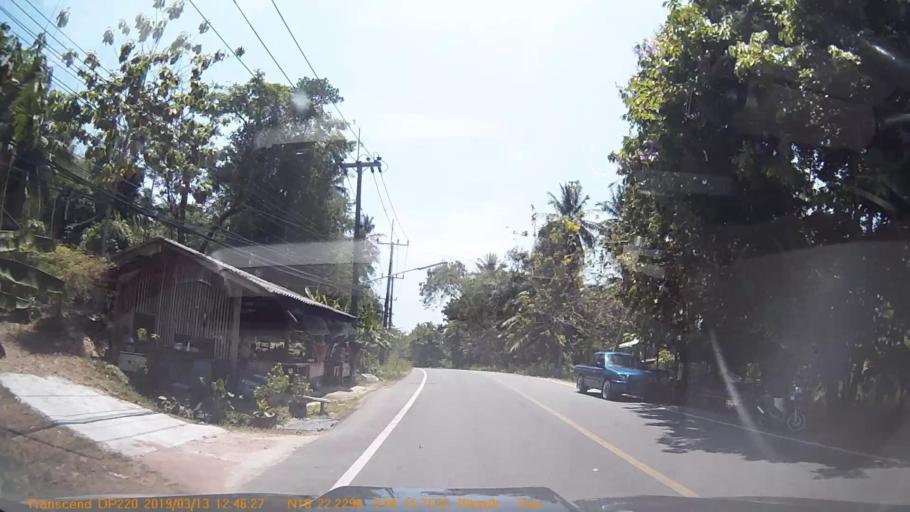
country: TH
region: Chumphon
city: Chumphon
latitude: 10.3701
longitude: 99.2625
